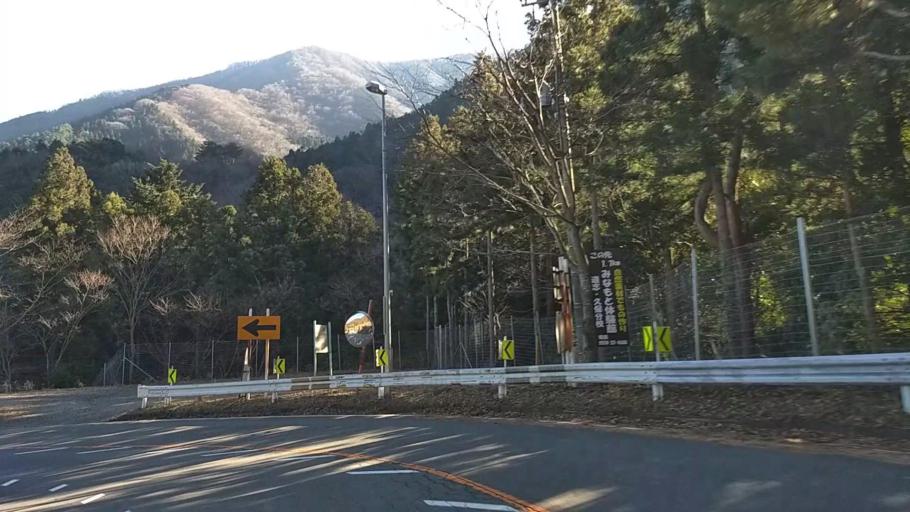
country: JP
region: Yamanashi
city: Uenohara
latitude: 35.5337
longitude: 139.0691
